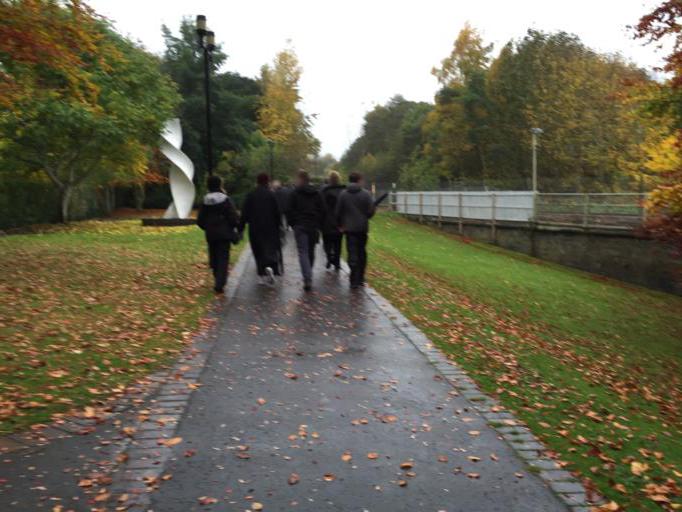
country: GB
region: Scotland
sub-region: Perth and Kinross
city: Perth
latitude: 56.3902
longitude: -3.4209
